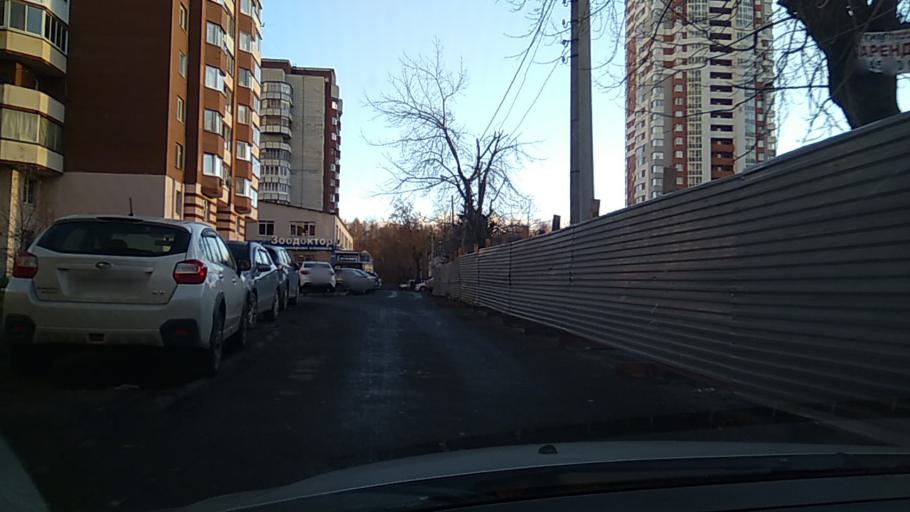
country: RU
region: Sverdlovsk
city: Sovkhoznyy
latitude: 56.7676
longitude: 60.6048
